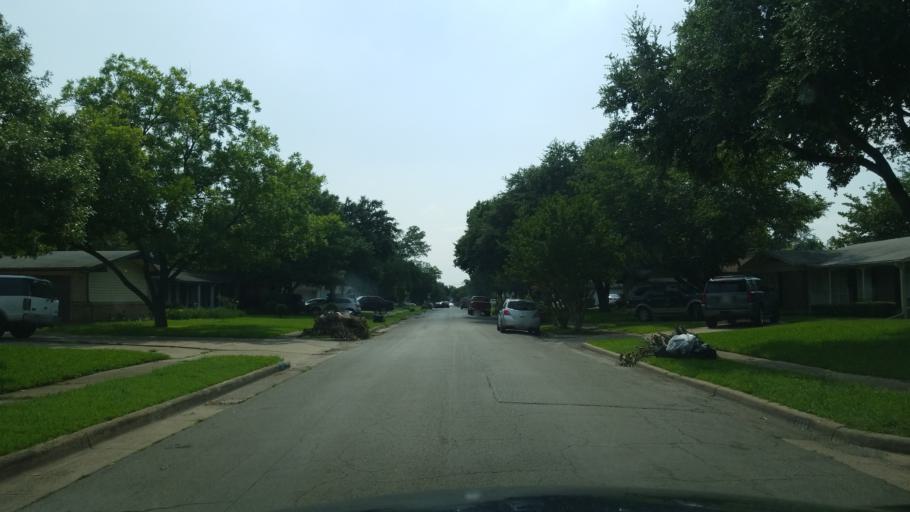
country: US
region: Texas
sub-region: Dallas County
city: Farmers Branch
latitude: 32.9022
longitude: -96.8763
